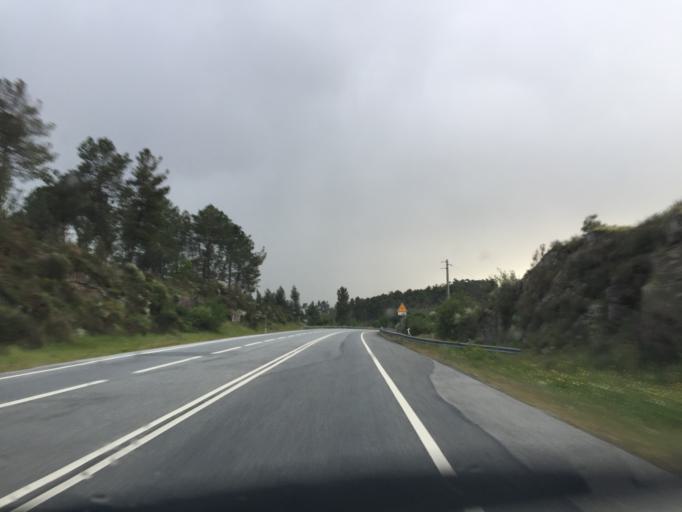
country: PT
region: Viseu
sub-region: Viseu
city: Viseu
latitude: 40.6089
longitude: -7.9624
